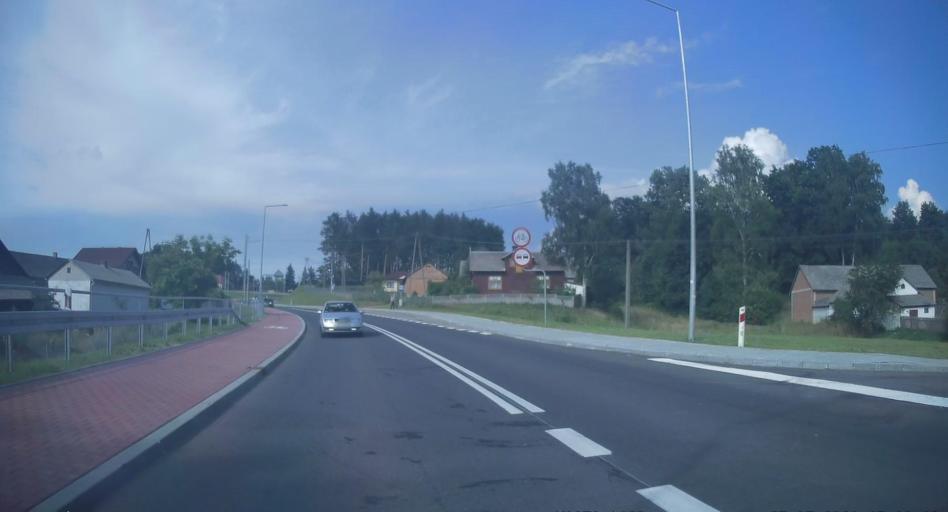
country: PL
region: Lodz Voivodeship
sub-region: Powiat tomaszowski
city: Inowlodz
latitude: 51.5548
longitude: 20.2557
